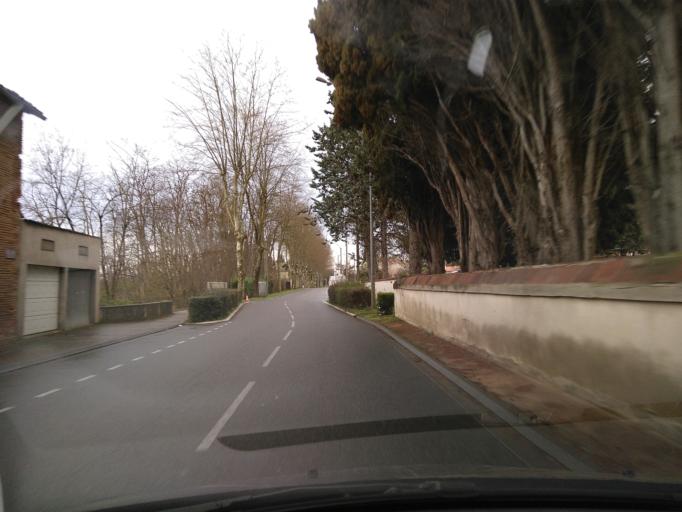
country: FR
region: Midi-Pyrenees
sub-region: Departement de la Haute-Garonne
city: Montesquieu-Volvestre
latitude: 43.2116
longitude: 1.2272
